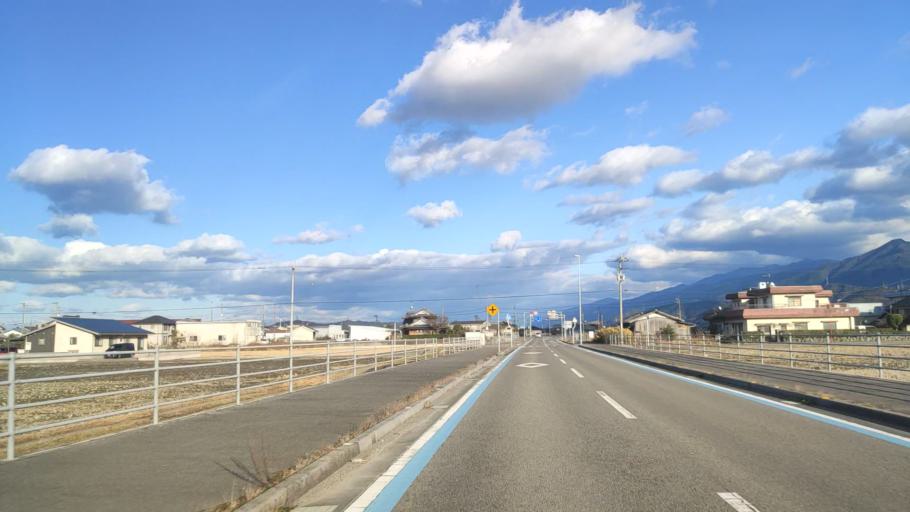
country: JP
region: Ehime
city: Saijo
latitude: 33.9085
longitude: 133.1540
